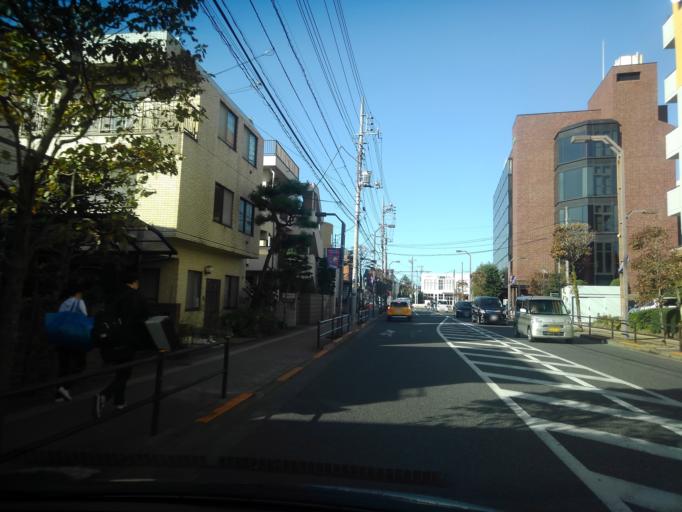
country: JP
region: Tokyo
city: Chofugaoka
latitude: 35.6517
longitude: 139.5569
